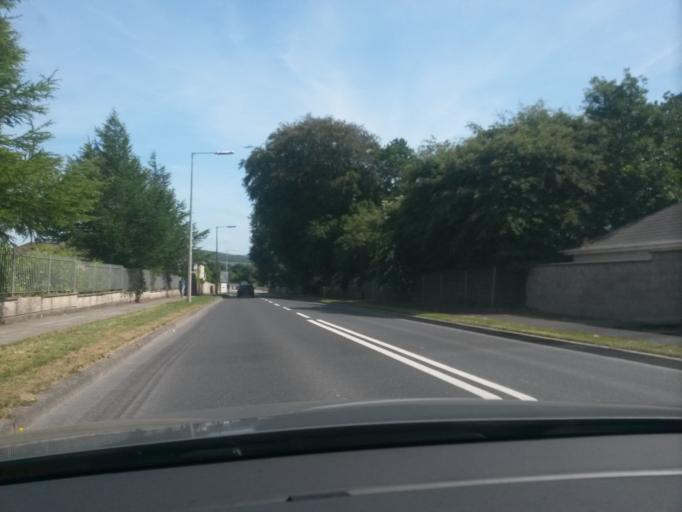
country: IE
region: Leinster
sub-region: Wicklow
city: Blessington
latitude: 53.1722
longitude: -6.5468
